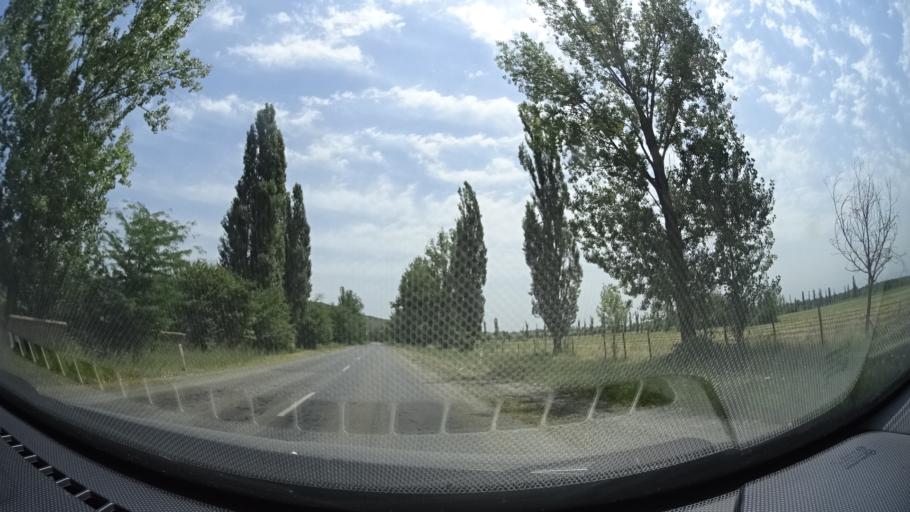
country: GE
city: Bagdadi
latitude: 41.8453
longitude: 46.0764
